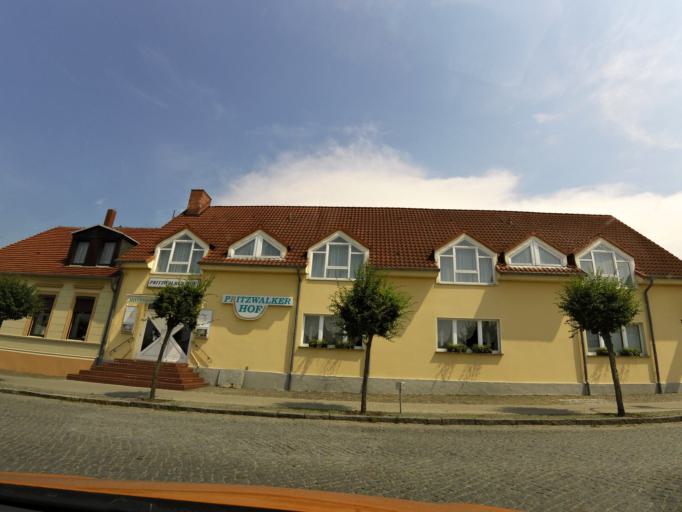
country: DE
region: Brandenburg
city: Pritzwalk
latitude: 53.1456
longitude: 12.1747
